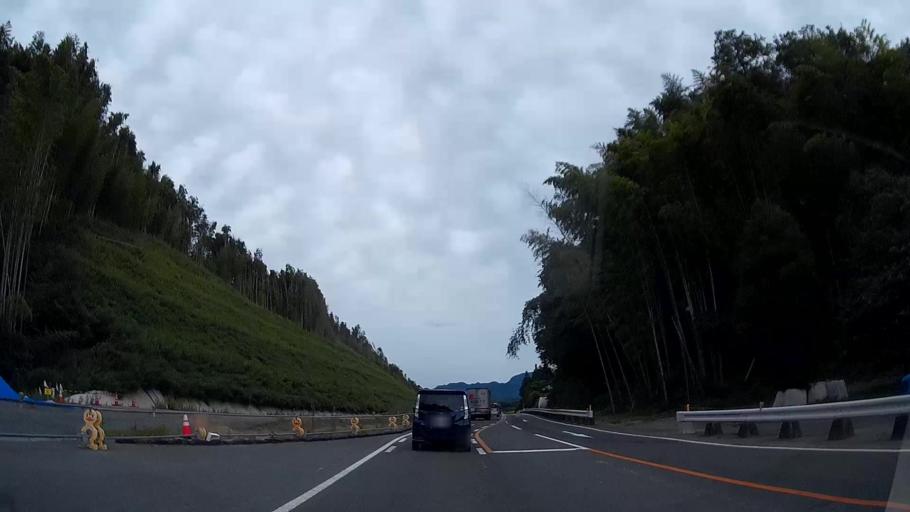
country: JP
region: Kumamoto
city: Kikuchi
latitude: 32.9546
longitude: 130.8218
